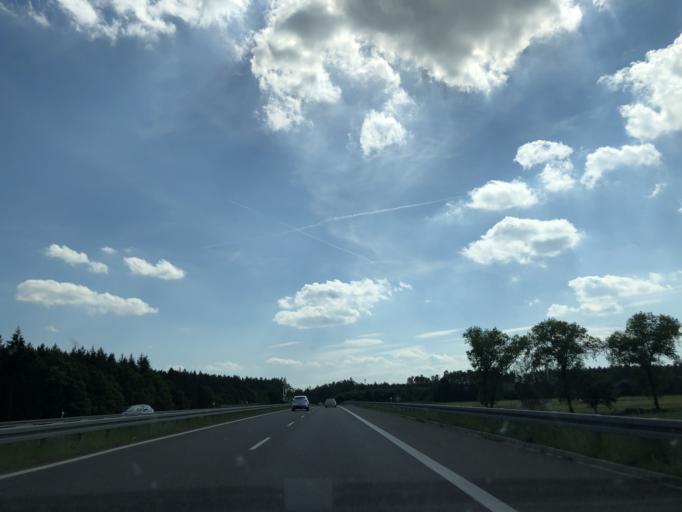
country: PL
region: West Pomeranian Voivodeship
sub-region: Powiat goleniowski
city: Nowogard
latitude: 53.6732
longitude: 15.0800
